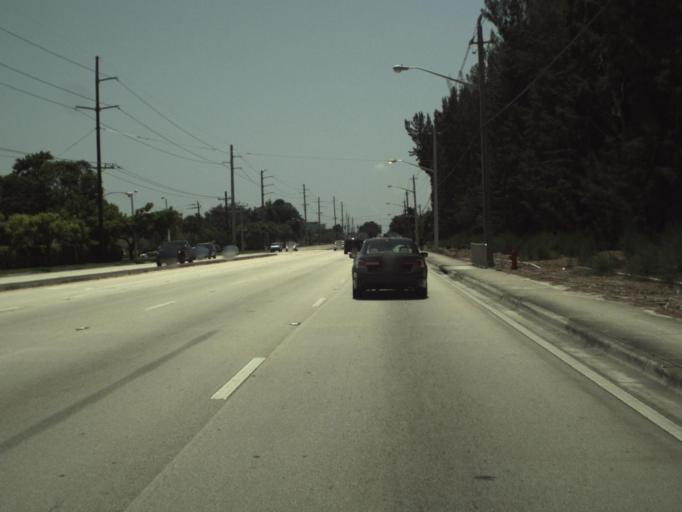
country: US
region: Florida
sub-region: Broward County
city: North Andrews Gardens
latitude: 26.2204
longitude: -80.1565
